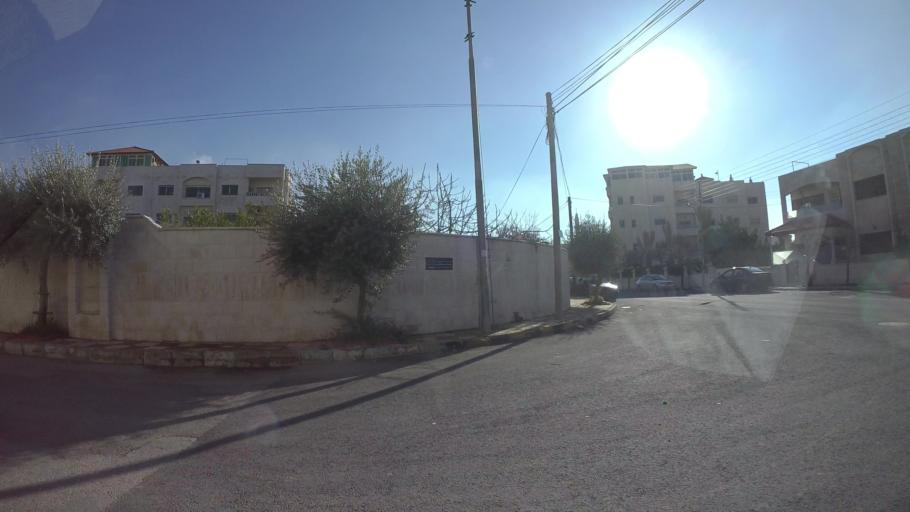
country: JO
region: Amman
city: Al Bunayyat ash Shamaliyah
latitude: 31.9013
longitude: 35.9209
